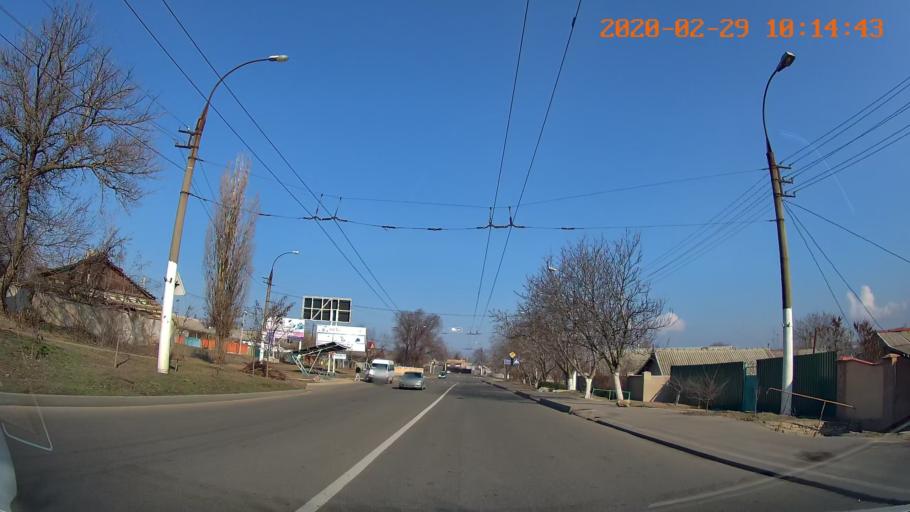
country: MD
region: Telenesti
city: Tiraspolul Nou
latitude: 46.8495
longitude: 29.6433
